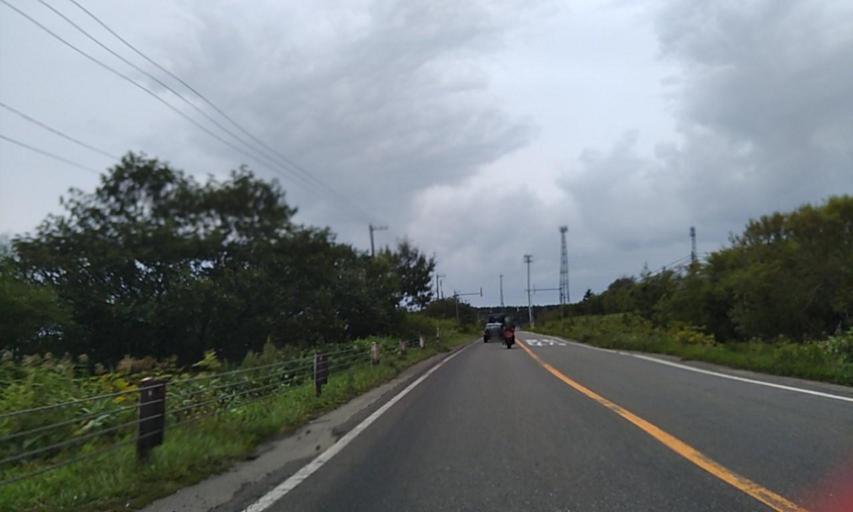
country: JP
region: Hokkaido
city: Nayoro
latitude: 44.9636
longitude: 142.5728
